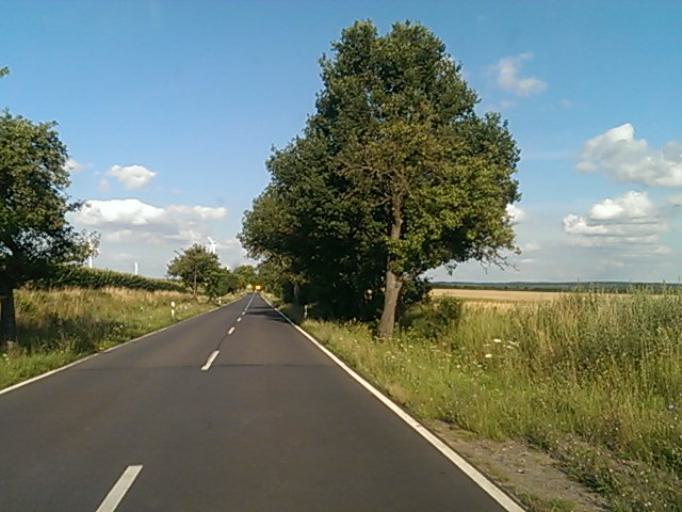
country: DE
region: Saxony-Anhalt
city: Nudersdorf
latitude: 51.9647
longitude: 12.5816
